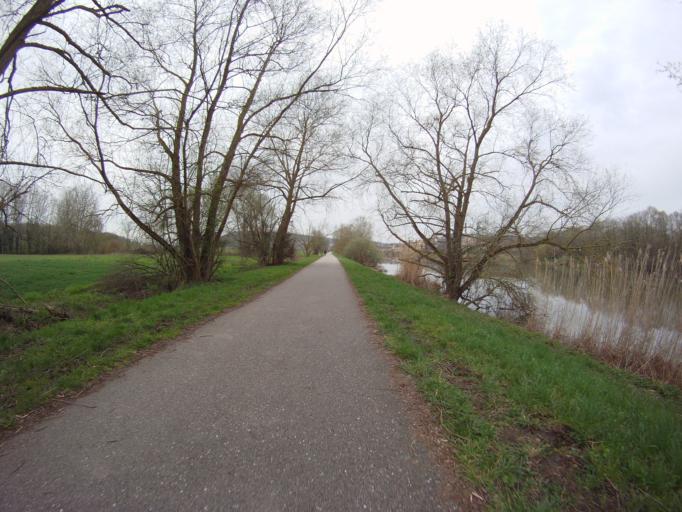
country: FR
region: Lorraine
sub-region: Departement de Meurthe-et-Moselle
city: Bouxieres-aux-Dames
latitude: 48.7413
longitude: 6.1784
